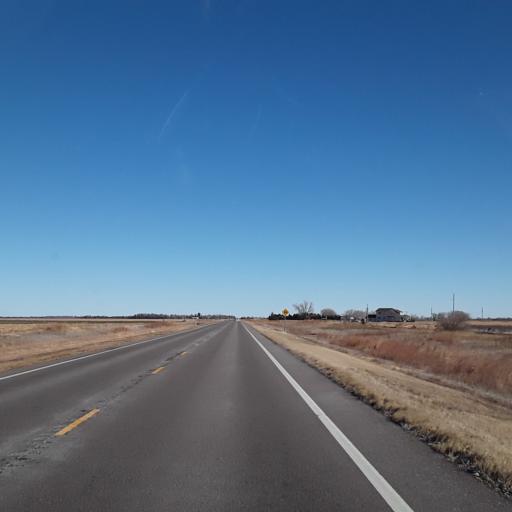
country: US
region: Kansas
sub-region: Pawnee County
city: Larned
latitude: 38.0999
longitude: -99.2082
